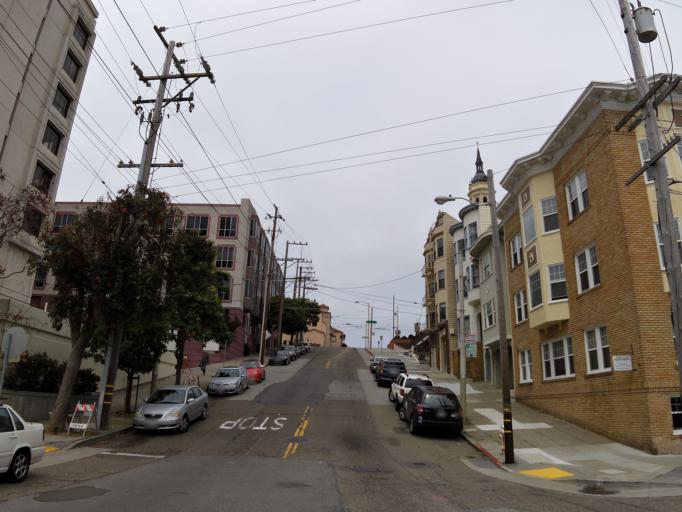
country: US
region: California
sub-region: San Francisco County
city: San Francisco
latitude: 37.7740
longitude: -122.4528
